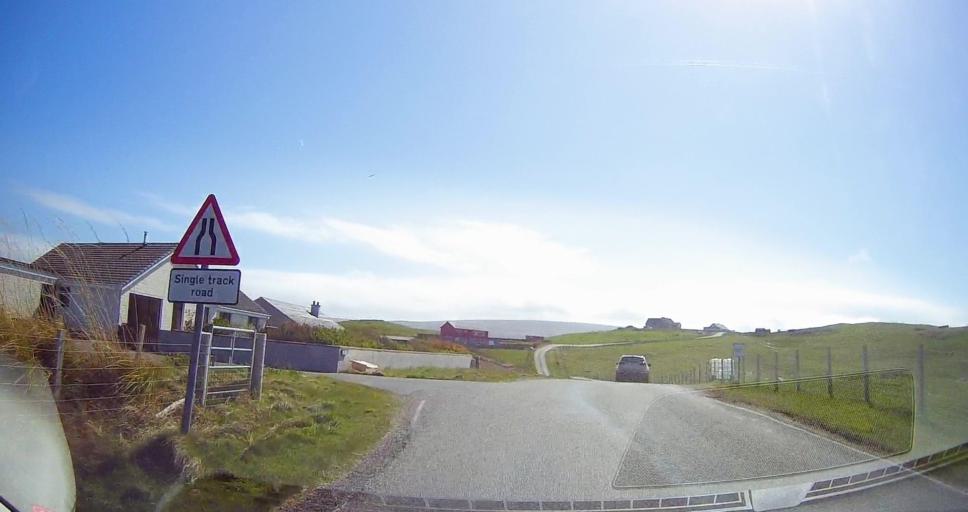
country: GB
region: Scotland
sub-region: Shetland Islands
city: Sandwick
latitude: 60.1028
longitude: -1.3253
